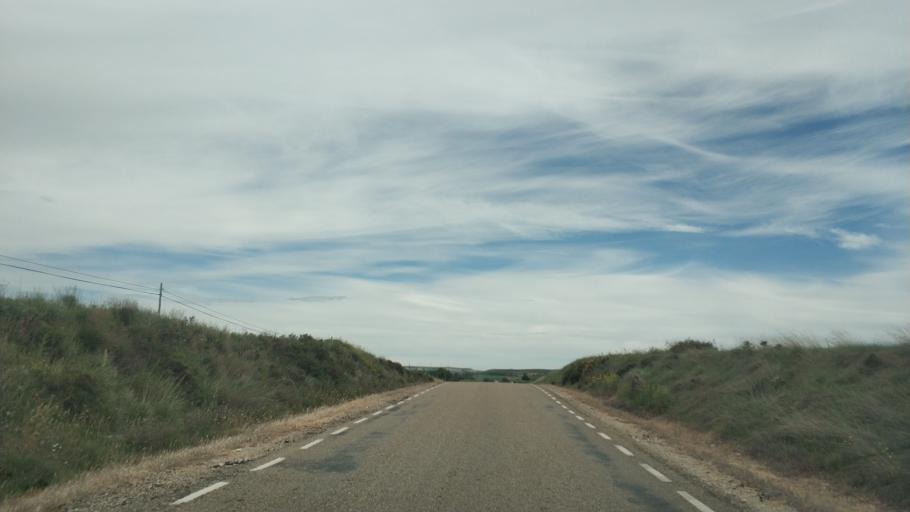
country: ES
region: Castille and Leon
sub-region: Provincia de Soria
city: Berlanga de Duero
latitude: 41.4566
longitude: -2.8520
